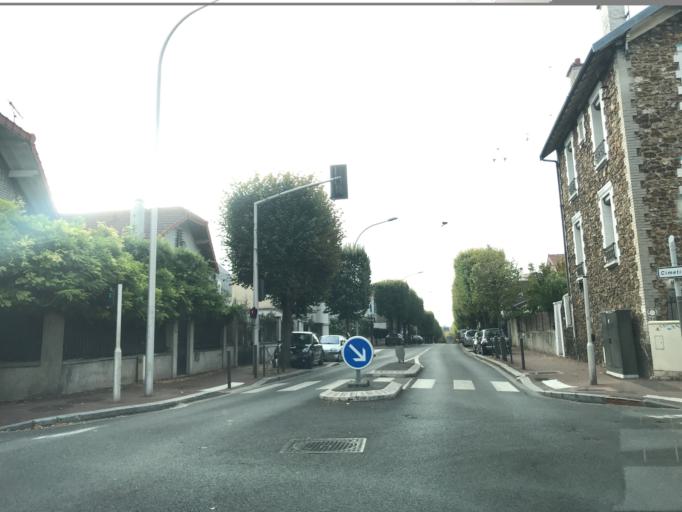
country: FR
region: Ile-de-France
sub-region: Departement du Val-de-Marne
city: Le Perreux-sur-Marne
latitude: 48.8469
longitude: 2.4967
